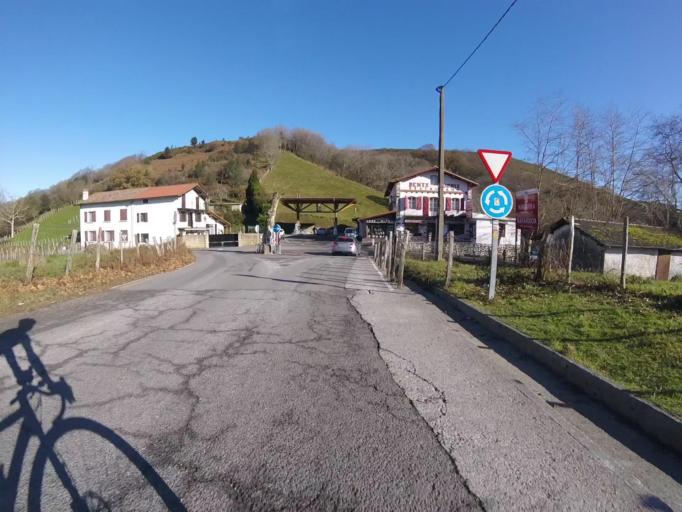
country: ES
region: Navarre
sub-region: Provincia de Navarra
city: Bera
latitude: 43.3095
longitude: -1.6847
